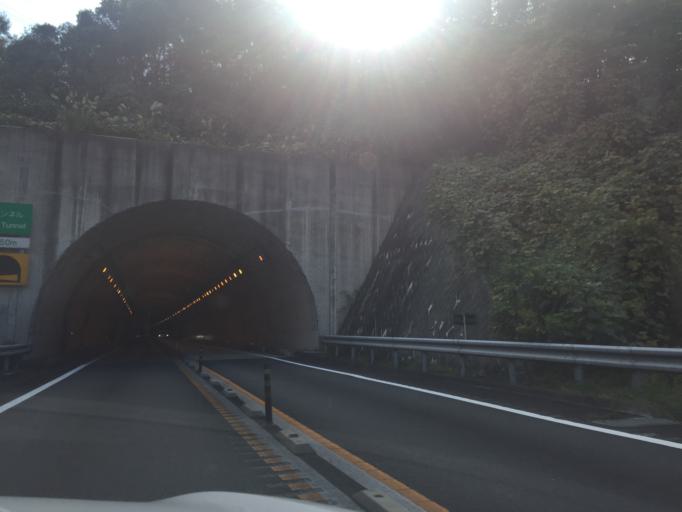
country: JP
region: Fukushima
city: Iwaki
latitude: 37.0839
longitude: 140.8418
